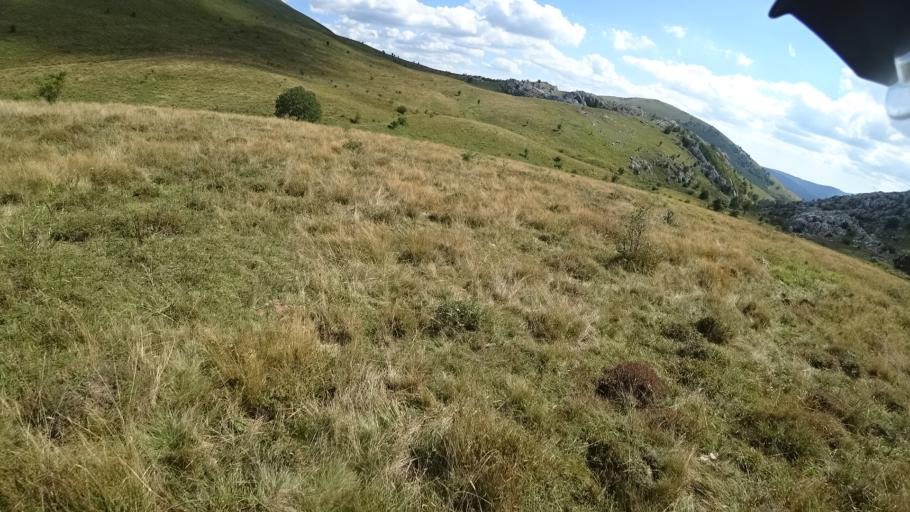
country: HR
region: Zadarska
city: Gracac
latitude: 44.4125
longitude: 16.0003
